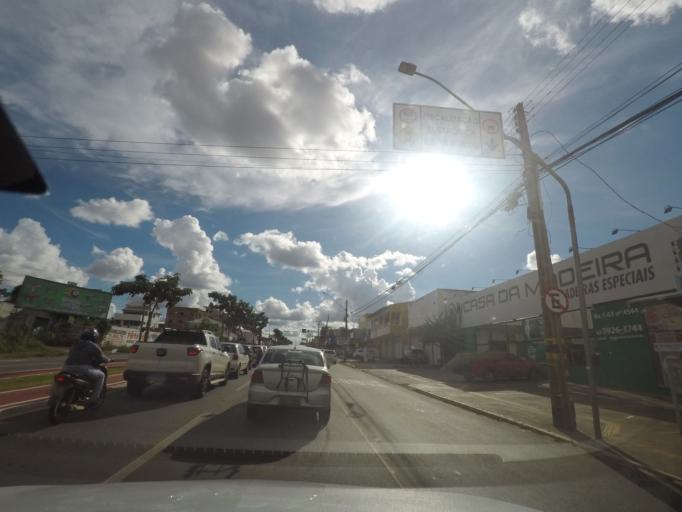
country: BR
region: Goias
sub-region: Goiania
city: Goiania
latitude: -16.7200
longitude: -49.3002
